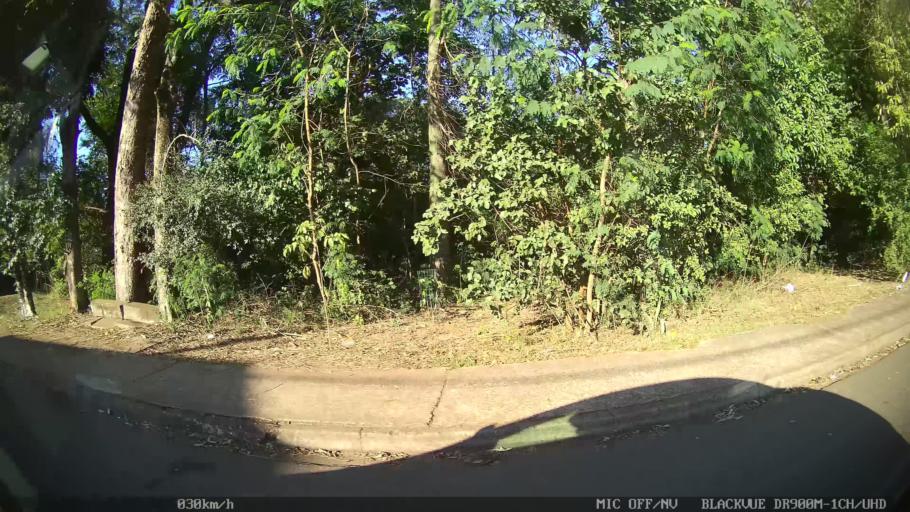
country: BR
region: Sao Paulo
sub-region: Piracicaba
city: Piracicaba
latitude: -22.6840
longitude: -47.6334
